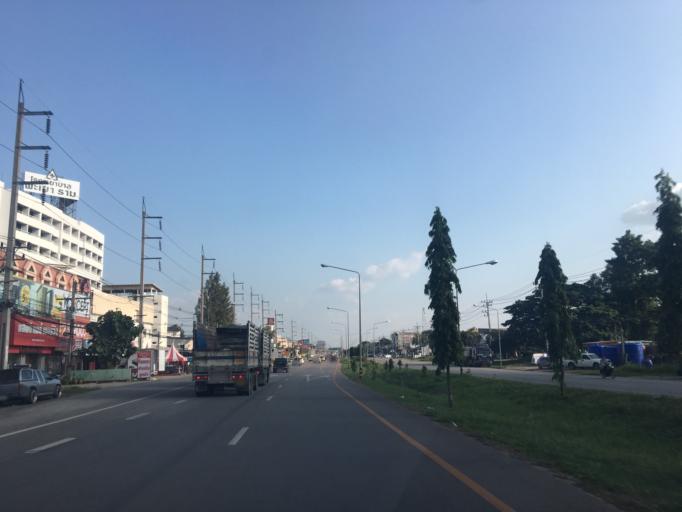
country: TH
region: Phayao
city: Phayao
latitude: 19.1789
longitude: 99.9003
